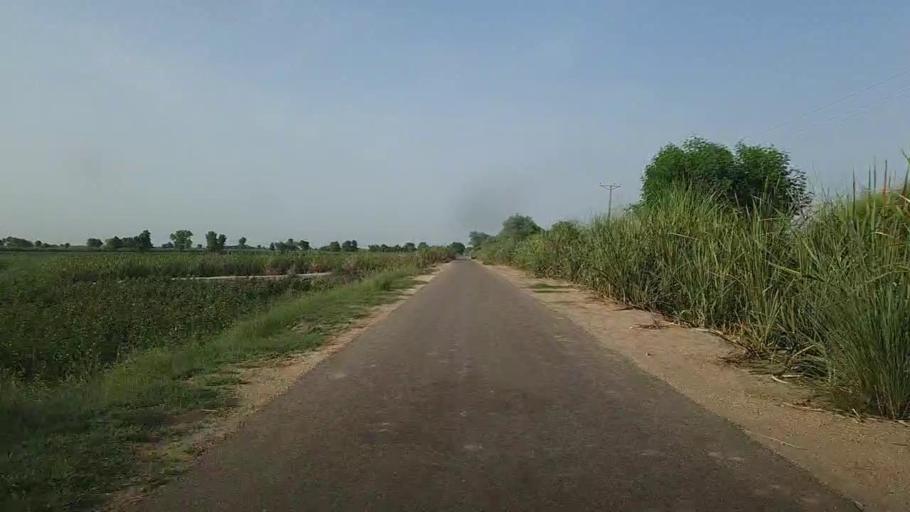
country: PK
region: Sindh
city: Ubauro
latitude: 28.0922
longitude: 69.8200
